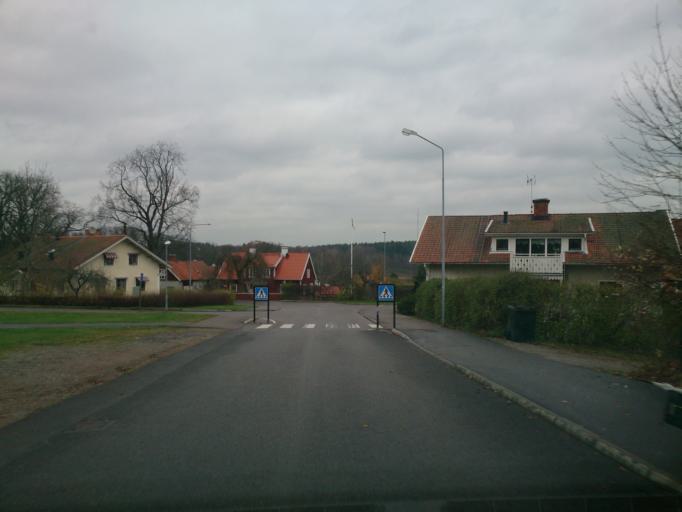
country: SE
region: OEstergoetland
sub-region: Atvidabergs Kommun
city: Atvidaberg
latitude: 58.1937
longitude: 16.0121
